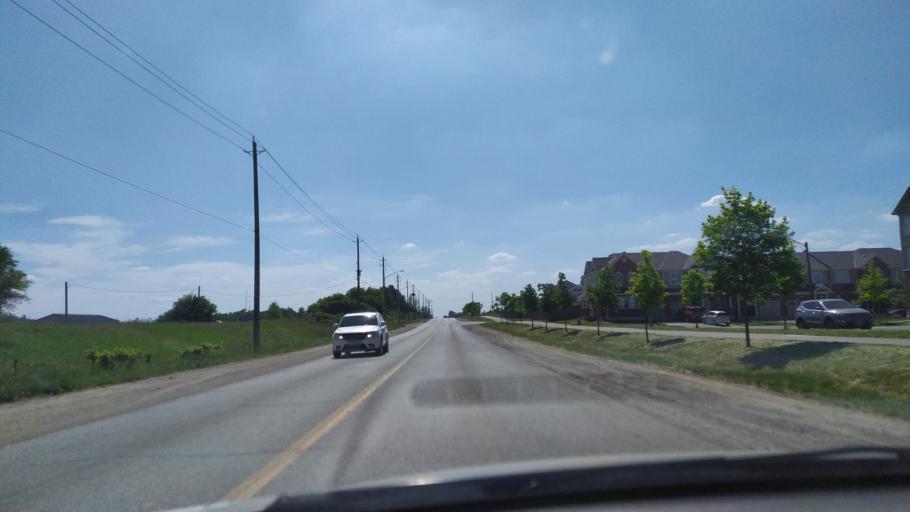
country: CA
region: Ontario
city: Kitchener
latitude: 43.3809
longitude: -80.4961
